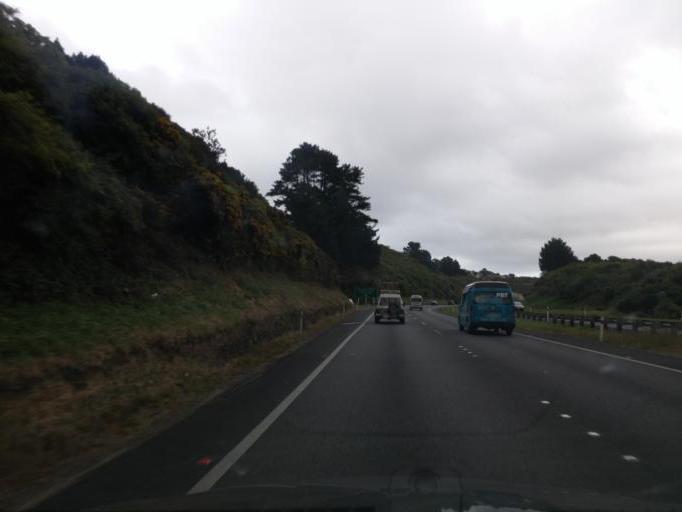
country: NZ
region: Wellington
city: Petone
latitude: -41.1992
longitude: 174.8243
